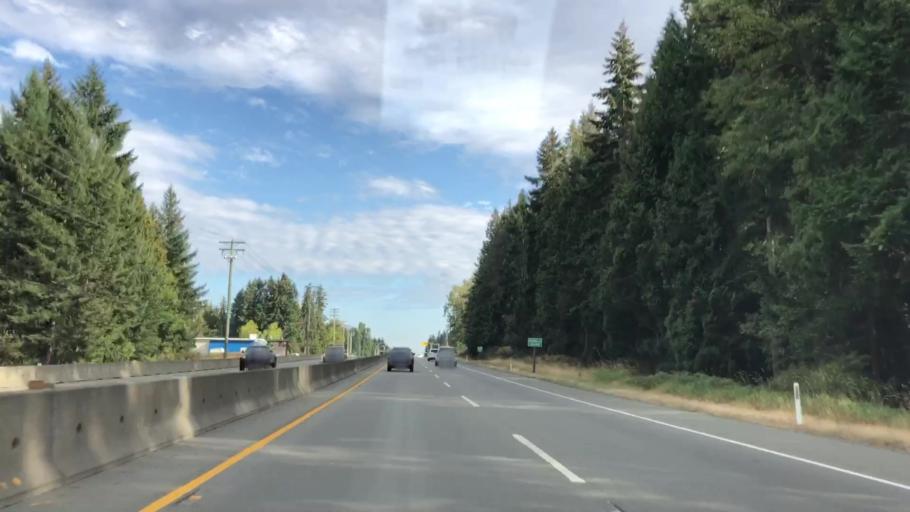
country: CA
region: British Columbia
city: Duncan
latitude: 48.6989
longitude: -123.5957
